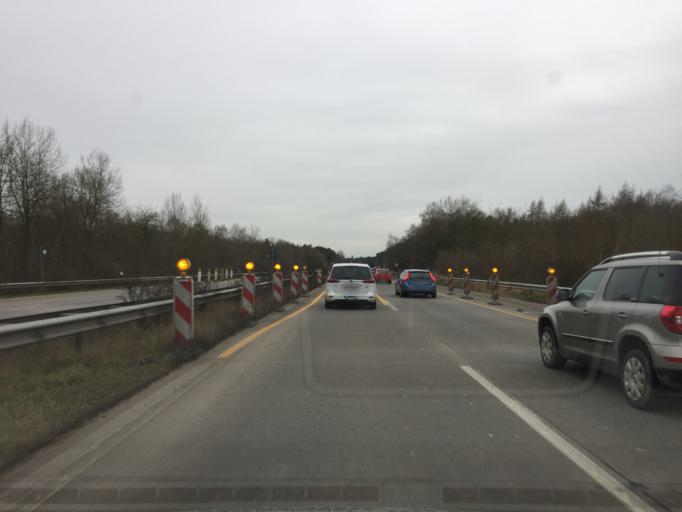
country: DE
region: Schleswig-Holstein
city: Ratekau
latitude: 53.9388
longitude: 10.7407
